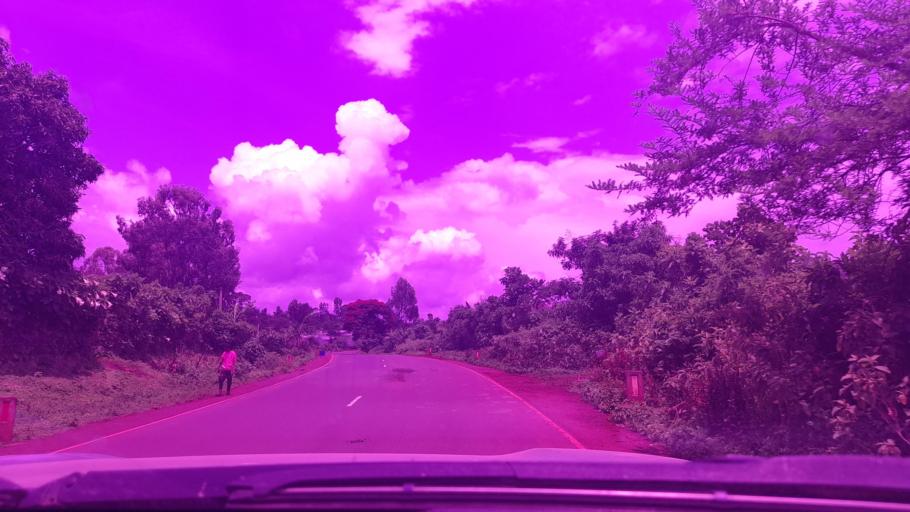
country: ET
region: Oromiya
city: Metu
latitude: 8.3361
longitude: 35.7301
